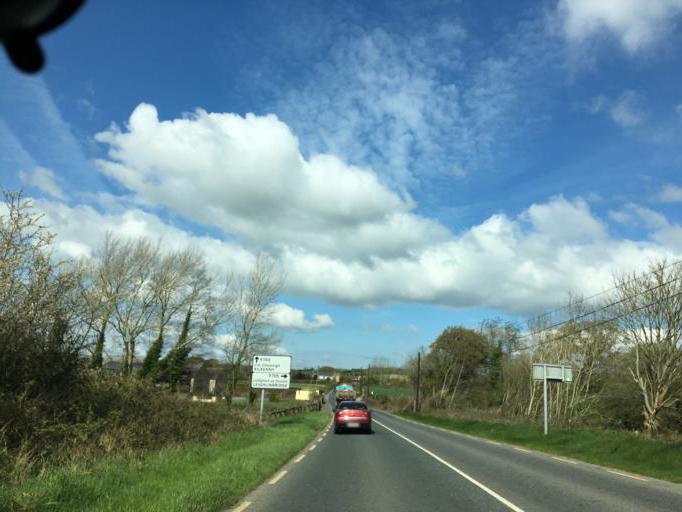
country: IE
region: Leinster
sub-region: Loch Garman
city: New Ross
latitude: 52.4332
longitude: -6.9554
